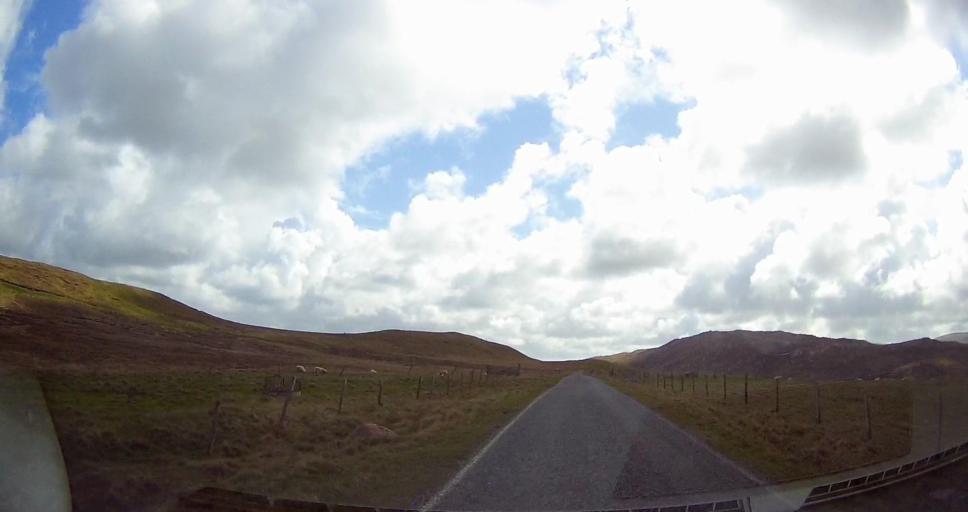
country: GB
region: Scotland
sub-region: Shetland Islands
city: Lerwick
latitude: 60.5612
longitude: -1.3341
